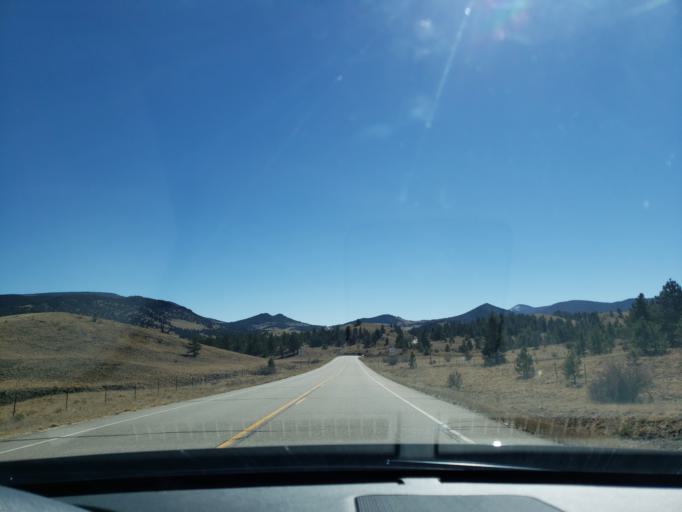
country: US
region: Colorado
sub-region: Chaffee County
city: Buena Vista
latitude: 38.8740
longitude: -105.6708
